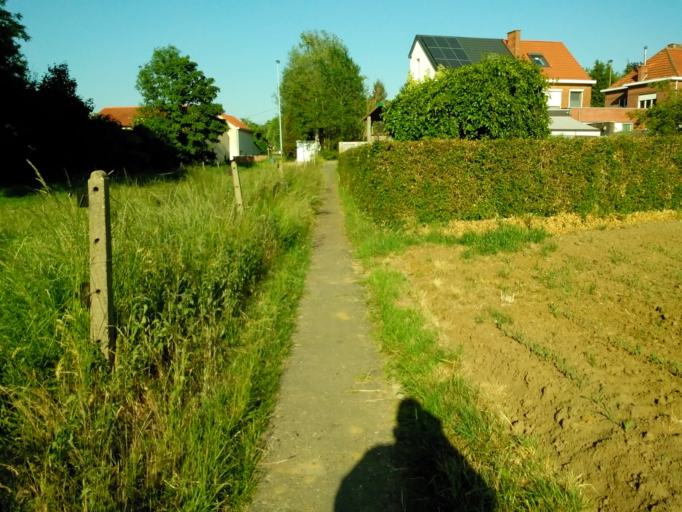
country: BE
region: Flanders
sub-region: Provincie Vlaams-Brabant
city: Holsbeek
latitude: 50.8934
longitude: 4.7503
